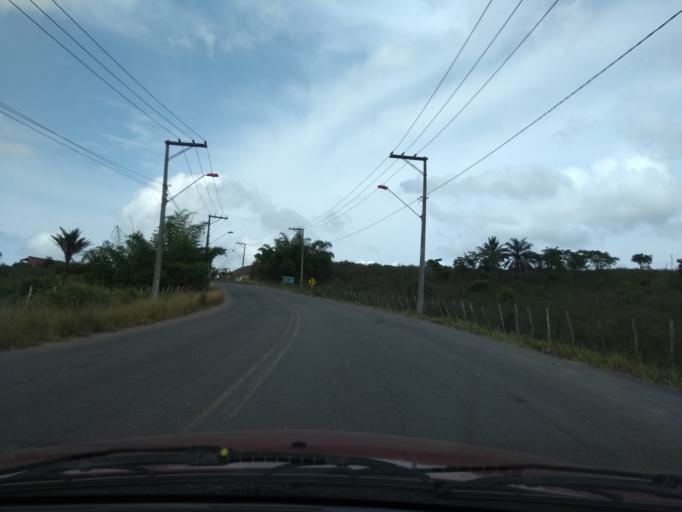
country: BR
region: Bahia
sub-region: Sao Francisco Do Conde
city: Sao Francisco do Conde
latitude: -12.6108
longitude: -38.6528
